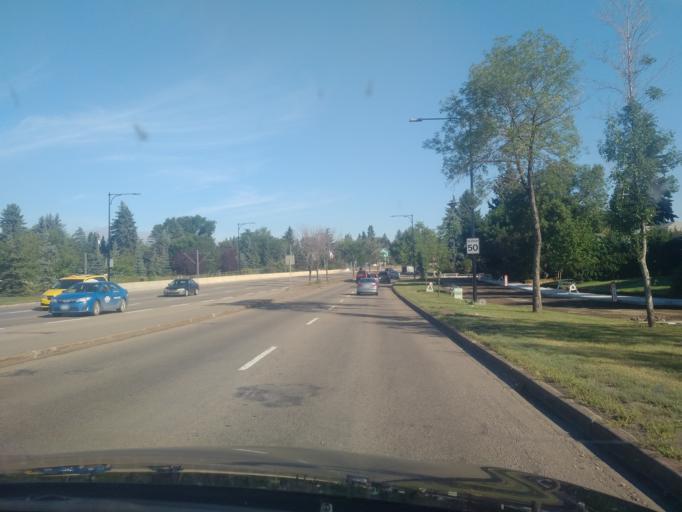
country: CA
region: Alberta
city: Edmonton
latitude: 53.5085
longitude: -113.5248
